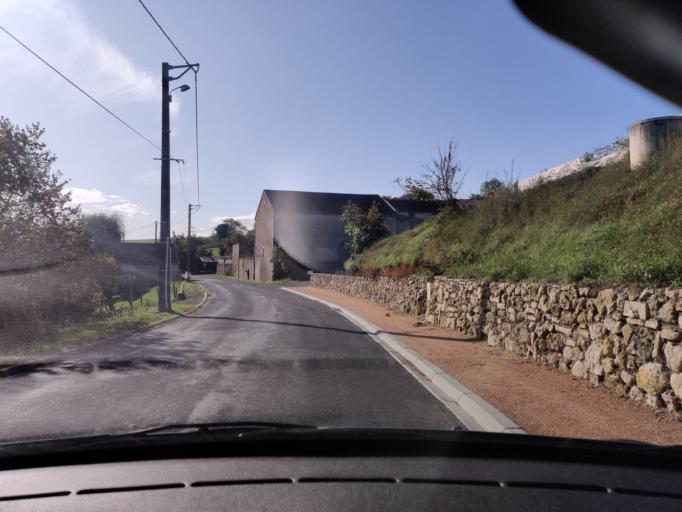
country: FR
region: Auvergne
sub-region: Departement du Puy-de-Dome
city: Aigueperse
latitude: 46.0320
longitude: 3.1654
